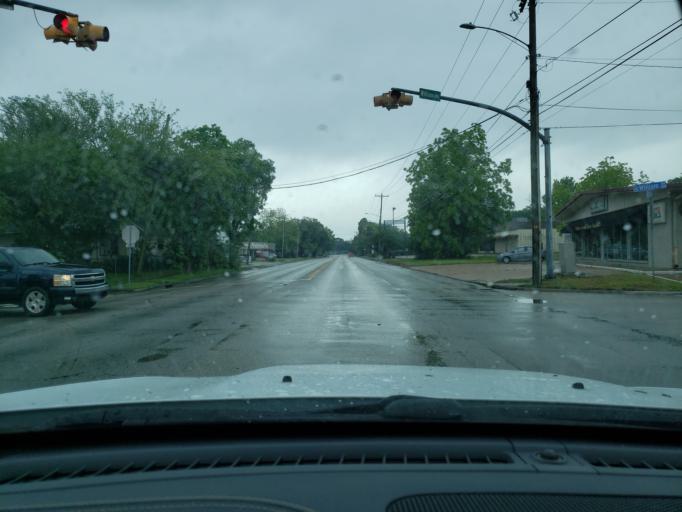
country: US
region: Texas
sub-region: Harris County
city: Baytown
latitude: 29.7441
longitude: -94.9721
